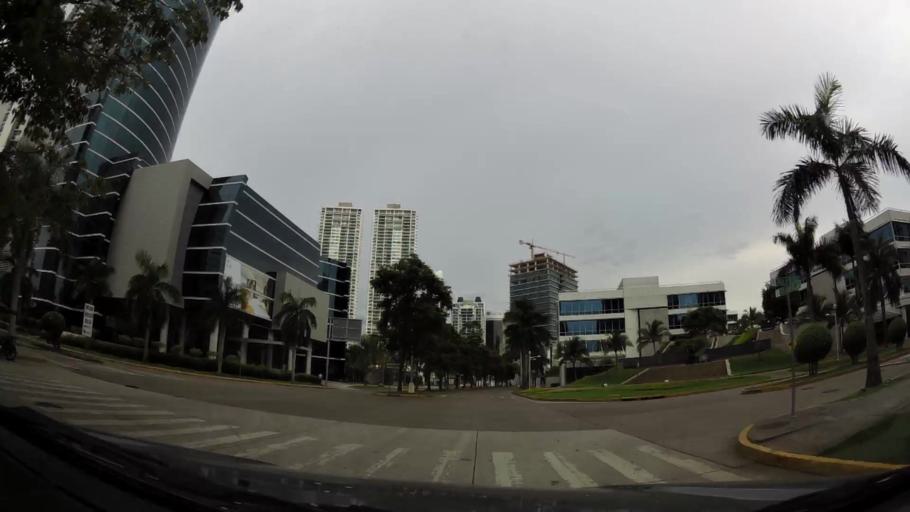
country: PA
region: Panama
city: San Miguelito
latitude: 9.0097
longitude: -79.4759
